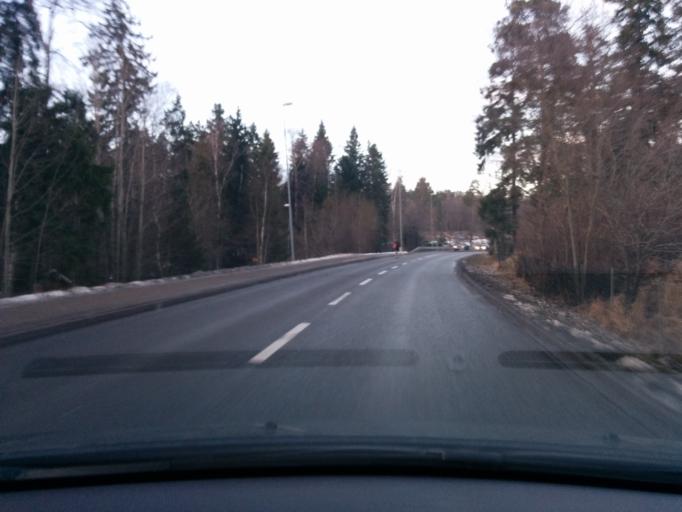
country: SE
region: Stockholm
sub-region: Nacka Kommun
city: Alta
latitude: 59.2744
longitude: 18.1756
